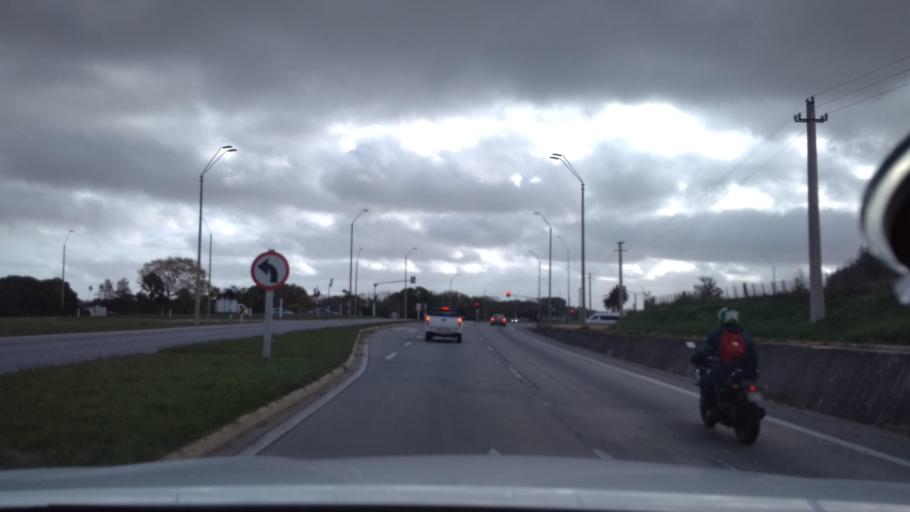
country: UY
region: Canelones
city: La Paz
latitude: -34.7834
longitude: -56.2510
